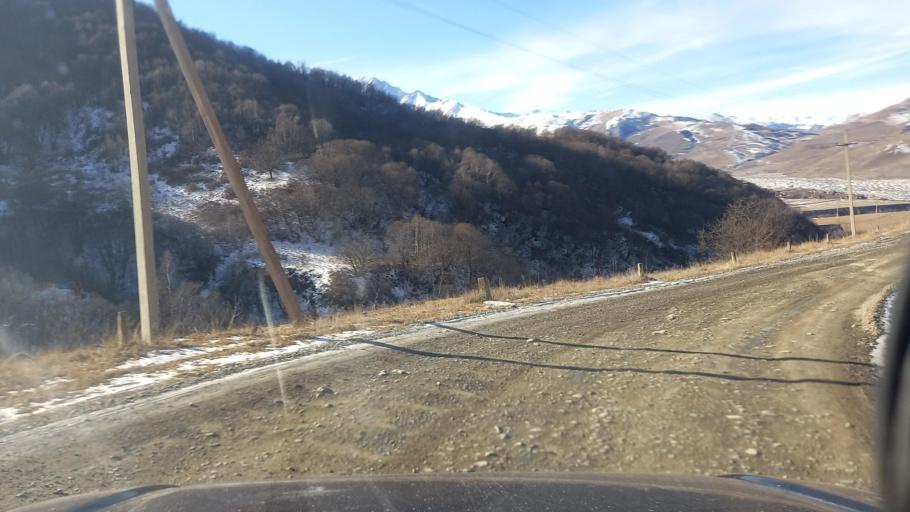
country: RU
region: North Ossetia
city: Verkhniy Fiagdon
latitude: 42.8383
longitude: 44.4645
